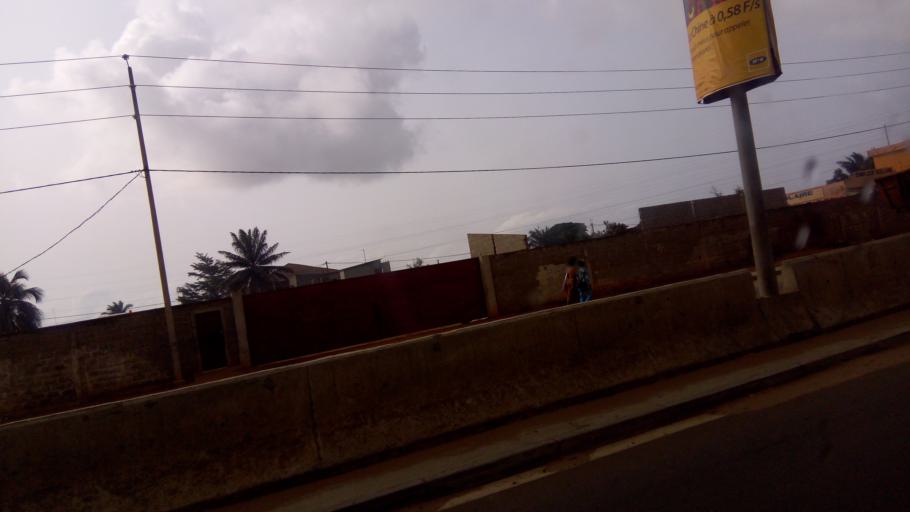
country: BJ
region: Atlantique
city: Abomey-Calavi
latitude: 6.3826
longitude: 2.3443
